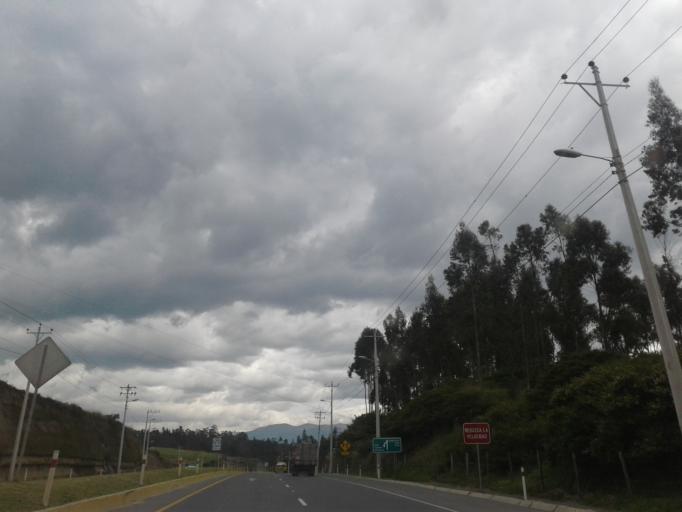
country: EC
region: Pichincha
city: Sangolqui
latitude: -0.3118
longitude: -78.3653
